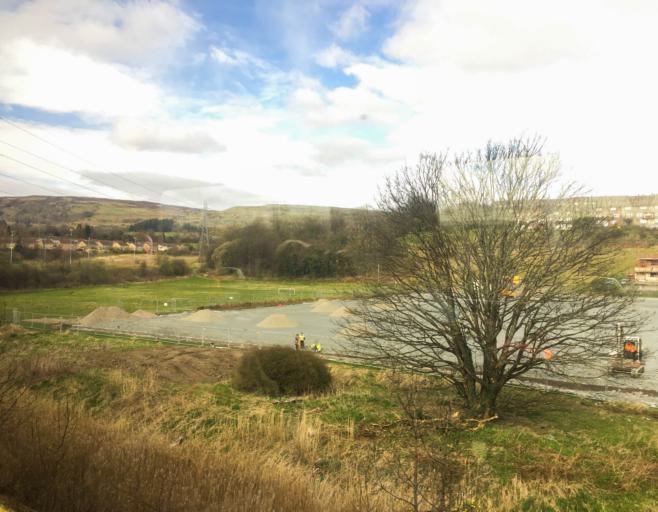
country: GB
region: Scotland
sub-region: West Dunbartonshire
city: Old Kilpatrick
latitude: 55.9171
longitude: -4.4389
